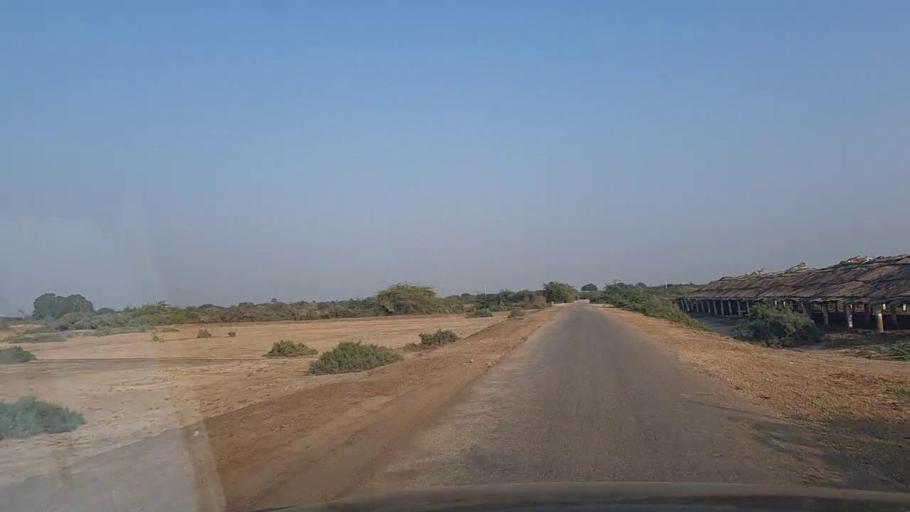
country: PK
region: Sindh
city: Keti Bandar
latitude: 24.2657
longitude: 67.5626
